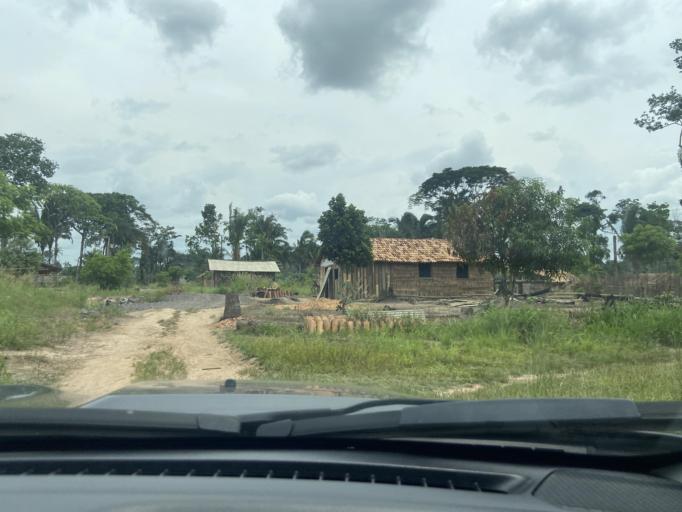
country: BR
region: Para
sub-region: Maraba
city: Maraba
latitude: -5.4224
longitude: -49.1115
